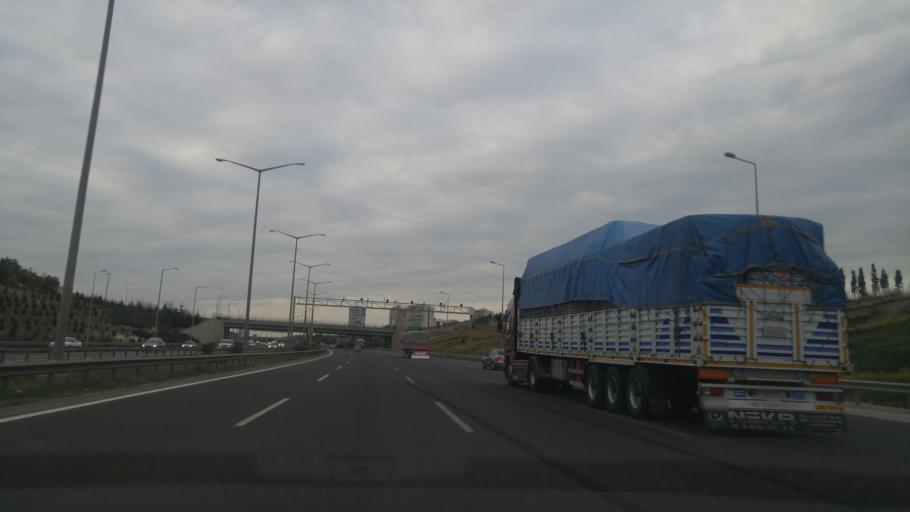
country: TR
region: Ankara
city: Etimesgut
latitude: 39.9945
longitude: 32.6373
